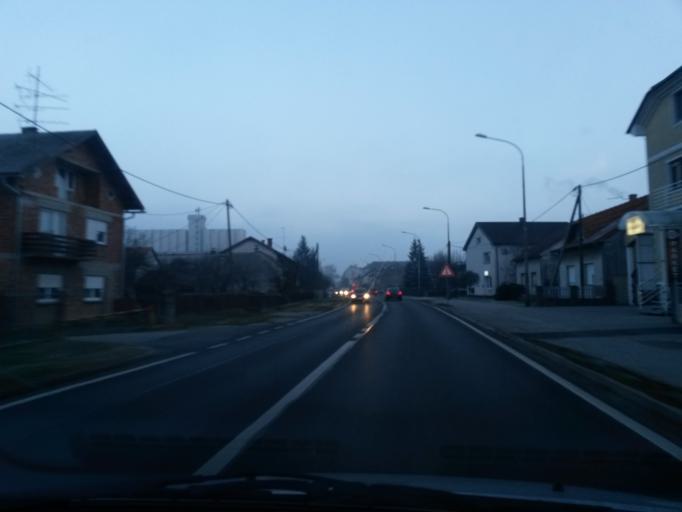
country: HR
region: Koprivnicko-Krizevacka
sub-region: Grad Koprivnica
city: Koprivnica
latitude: 46.1694
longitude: 16.8153
